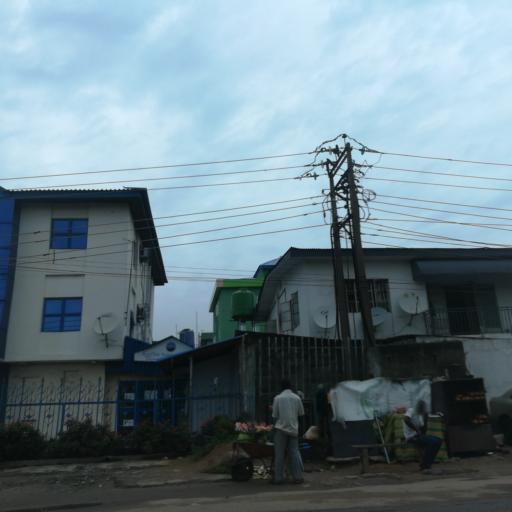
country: NG
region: Lagos
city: Ikeja
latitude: 6.5960
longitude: 3.3473
